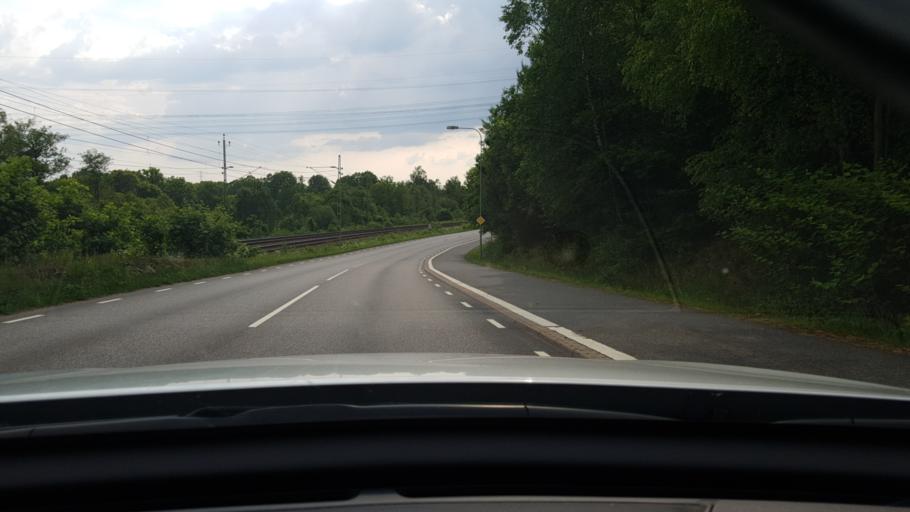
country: SE
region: Vaestra Goetaland
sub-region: Lerums Kommun
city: Stenkullen
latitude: 57.8035
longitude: 12.3471
